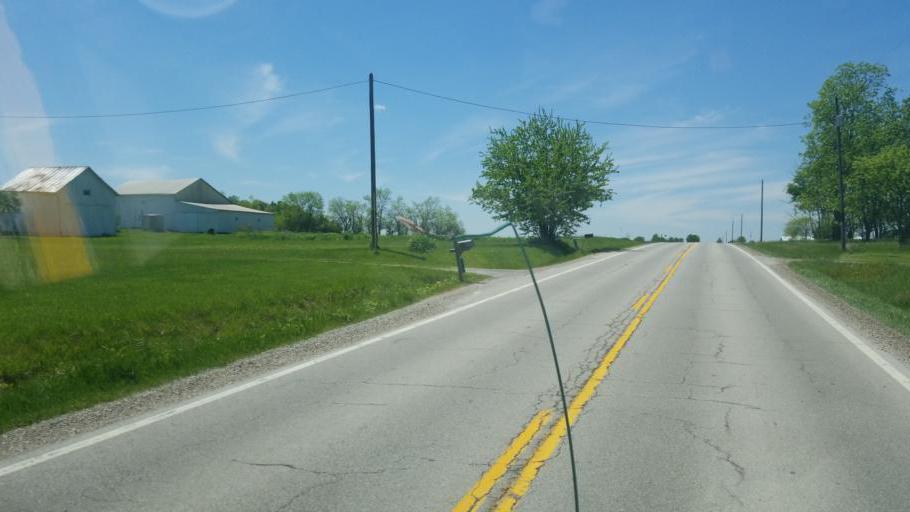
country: US
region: Ohio
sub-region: Huron County
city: Greenwich
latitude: 41.0294
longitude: -82.4565
